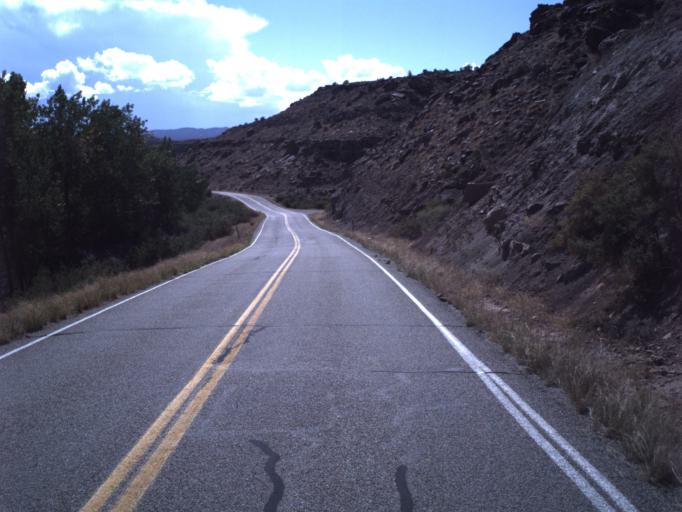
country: US
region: Utah
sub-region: Grand County
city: Moab
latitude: 38.8311
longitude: -109.2871
